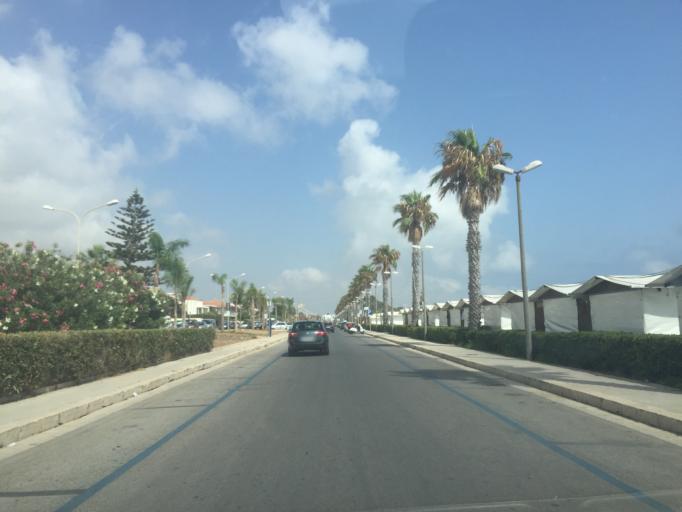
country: IT
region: Sicily
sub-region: Ragusa
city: Marina di Ragusa
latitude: 36.7816
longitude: 14.5628
